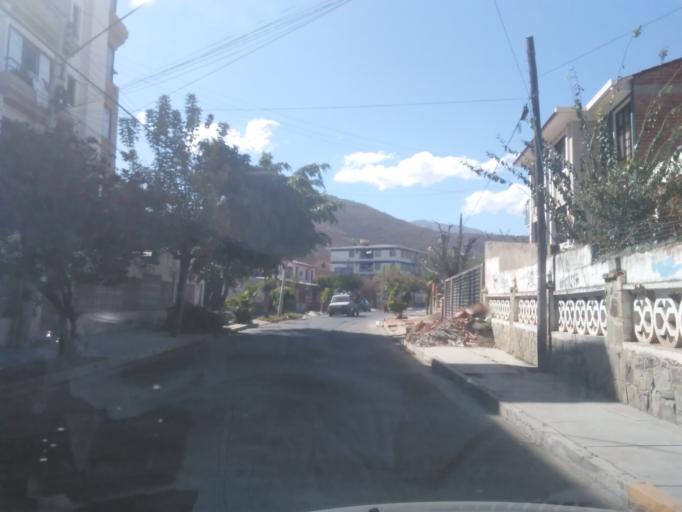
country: BO
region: Cochabamba
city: Cochabamba
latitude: -17.3955
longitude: -66.1426
